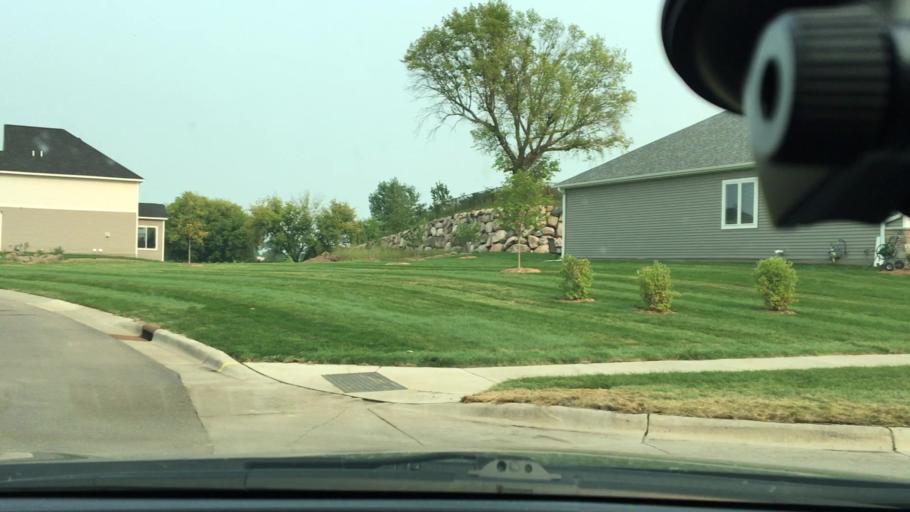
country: US
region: Minnesota
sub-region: Wright County
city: Otsego
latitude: 45.2600
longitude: -93.5715
